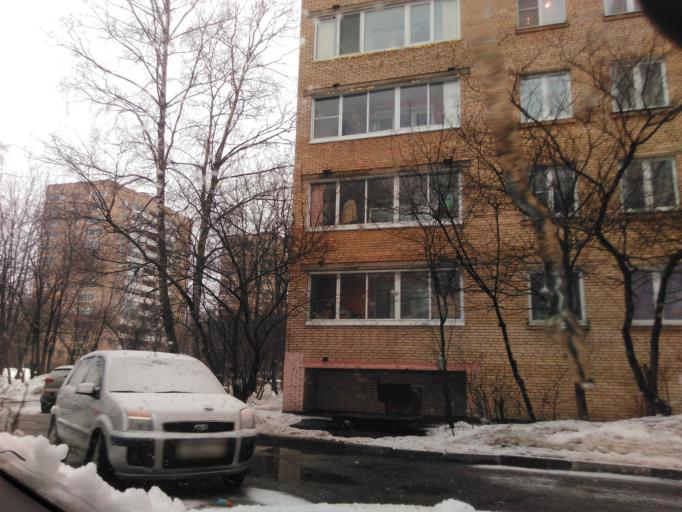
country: RU
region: Moskovskaya
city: Rzhavki
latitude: 56.0002
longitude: 37.2360
